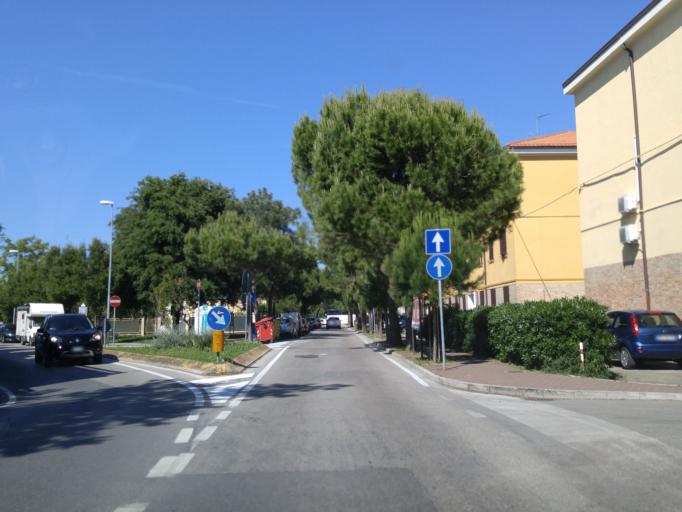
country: IT
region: The Marches
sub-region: Provincia di Pesaro e Urbino
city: Pesaro
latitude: 43.9171
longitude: 12.9060
